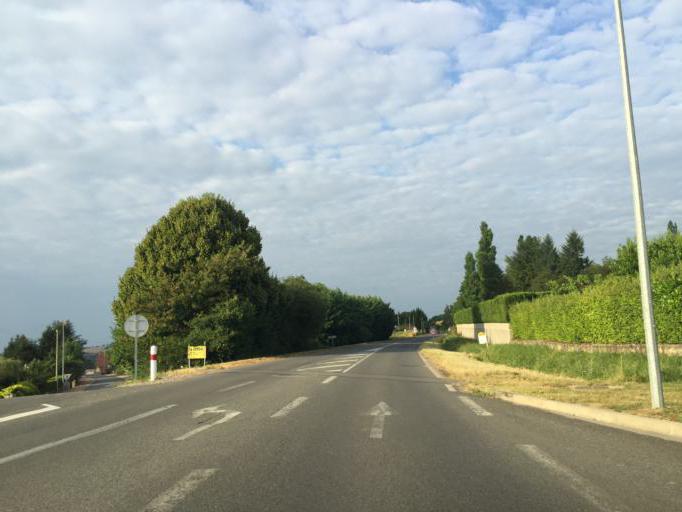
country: FR
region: Auvergne
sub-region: Departement de l'Allier
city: Saint-Remy-en-Rollat
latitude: 46.1823
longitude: 3.4195
